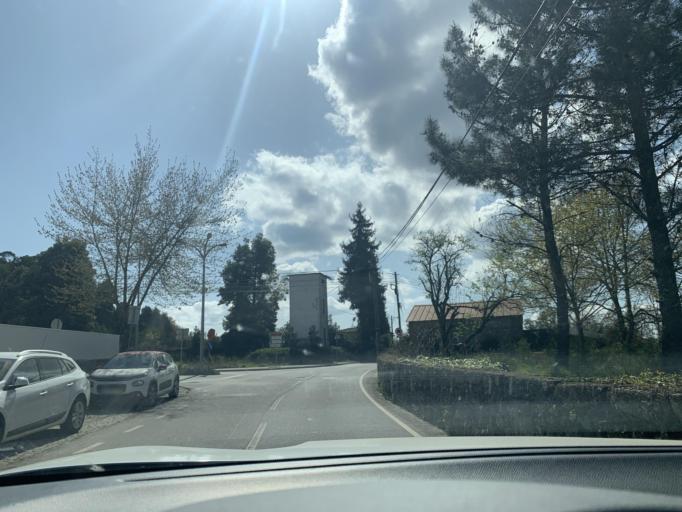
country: PT
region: Viseu
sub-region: Viseu
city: Rio de Loba
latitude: 40.6969
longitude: -7.8691
